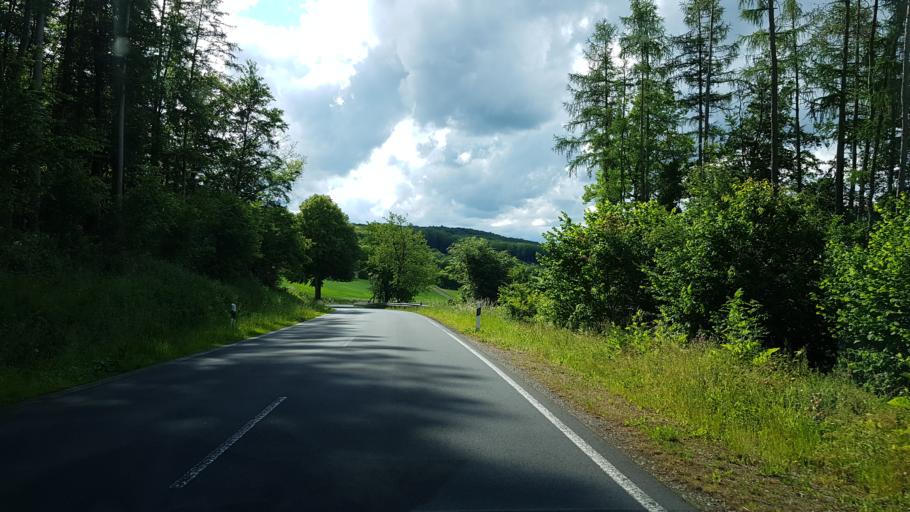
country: DE
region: Lower Saxony
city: Moringen
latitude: 51.7328
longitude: 9.8910
